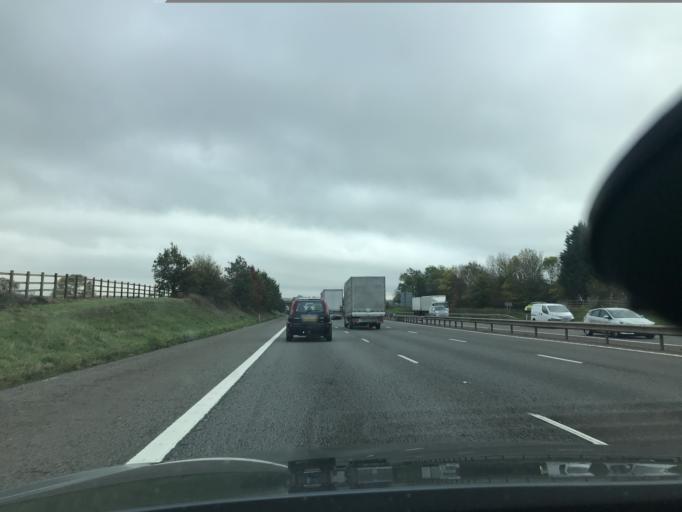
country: GB
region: England
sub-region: Warwickshire
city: Warwick
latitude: 52.2354
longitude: -1.5413
